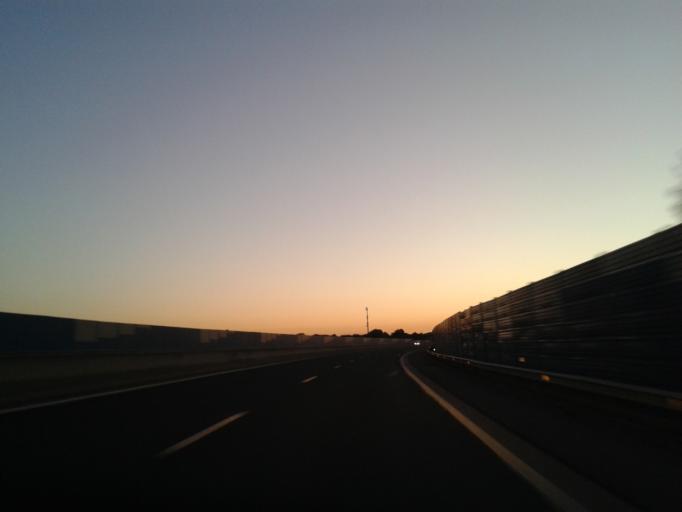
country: PT
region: Faro
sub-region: Albufeira
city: Guia
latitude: 37.1391
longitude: -8.2813
